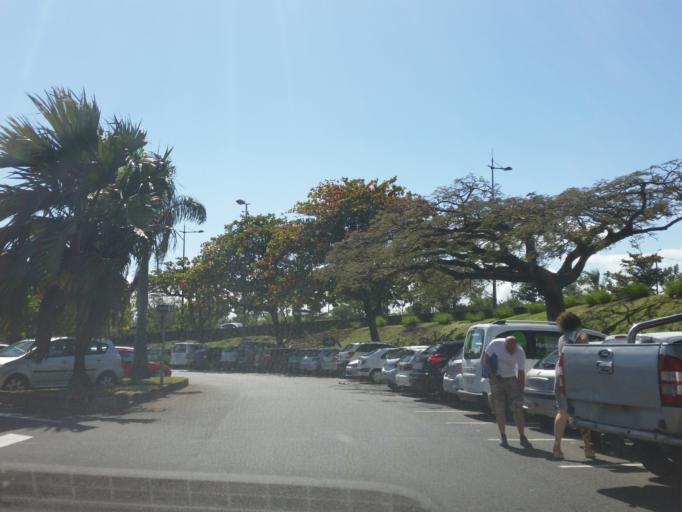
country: RE
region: Reunion
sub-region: Reunion
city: Sainte-Marie
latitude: -20.8932
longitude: 55.5012
